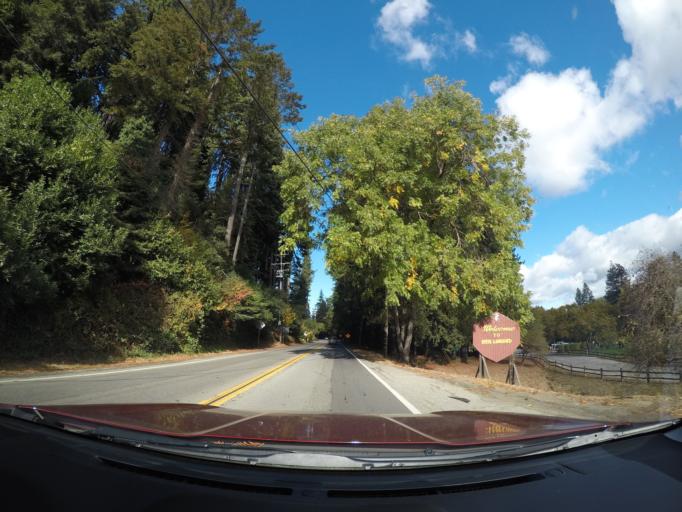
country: US
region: California
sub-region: Santa Cruz County
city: Ben Lomond
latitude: 37.0797
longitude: -122.0836
